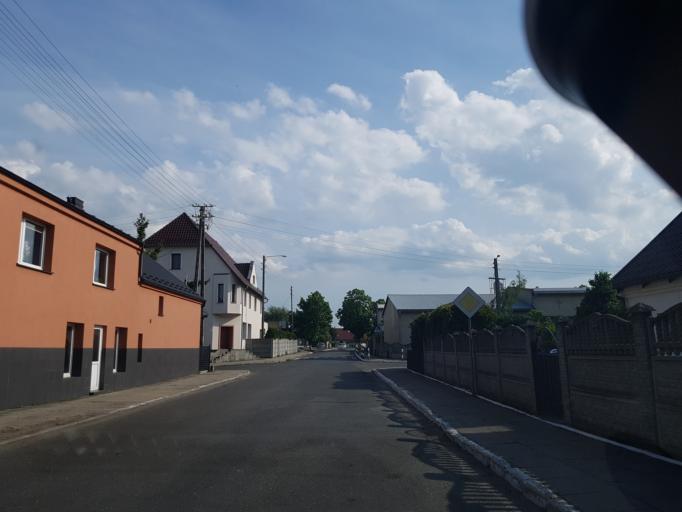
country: PL
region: Lower Silesian Voivodeship
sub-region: Powiat olawski
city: Wierzbno
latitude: 50.8944
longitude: 17.1308
